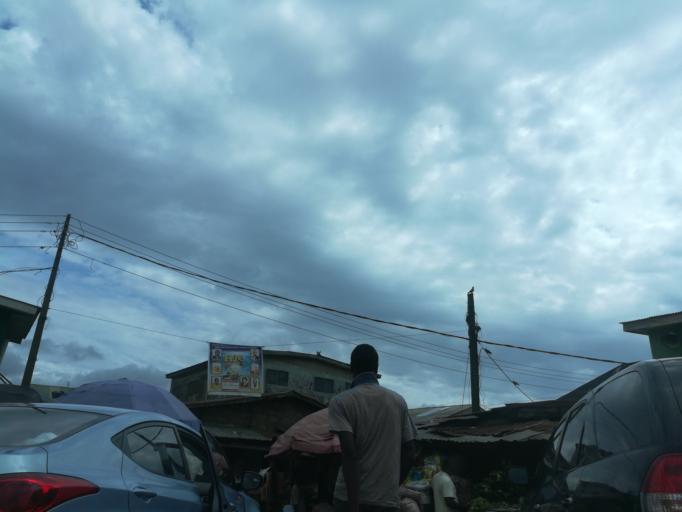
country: NG
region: Lagos
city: Agege
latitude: 6.6240
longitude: 3.3275
